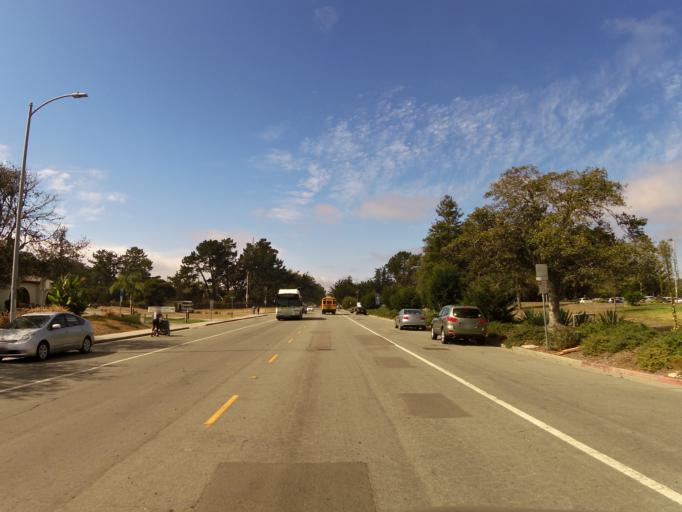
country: US
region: California
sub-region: Santa Cruz County
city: Santa Cruz
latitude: 36.9549
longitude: -122.0538
